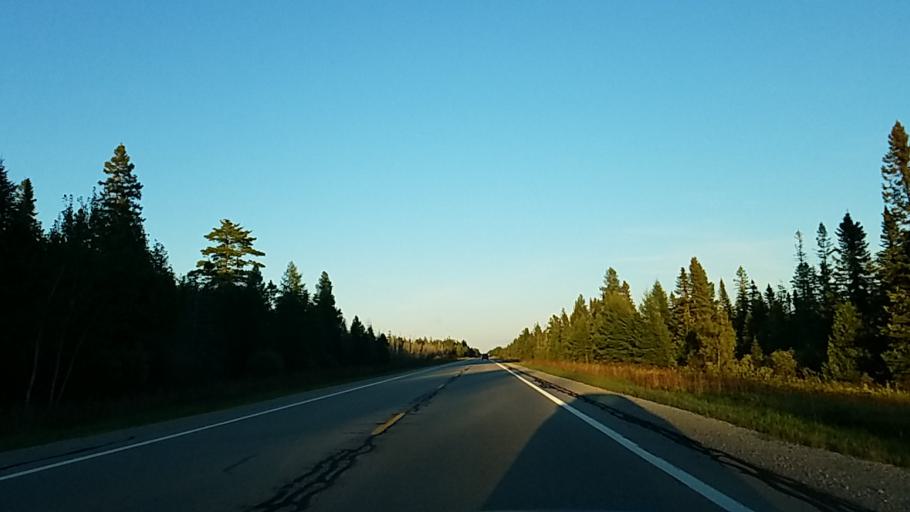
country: US
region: Michigan
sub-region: Alger County
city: Munising
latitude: 46.3467
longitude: -86.3786
